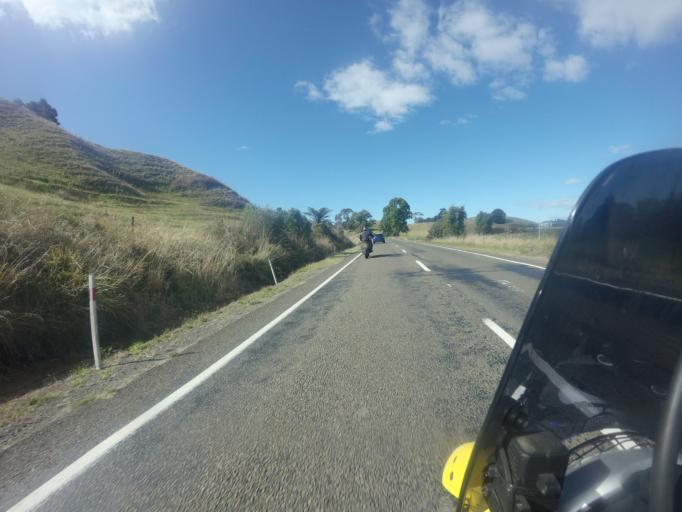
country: NZ
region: Bay of Plenty
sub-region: Opotiki District
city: Opotiki
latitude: -38.0366
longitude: 177.1646
